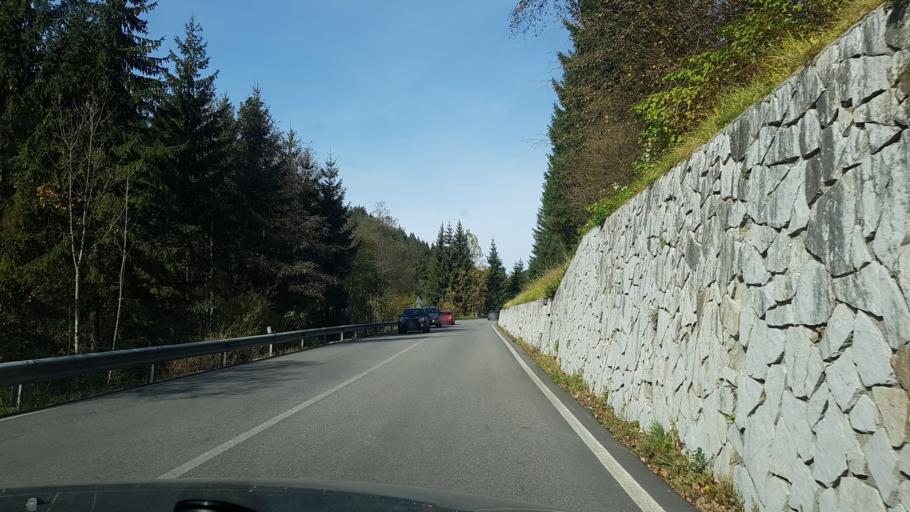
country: IT
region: Veneto
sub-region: Provincia di Belluno
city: Santo Stefano di Cadore
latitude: 46.5682
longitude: 12.5388
